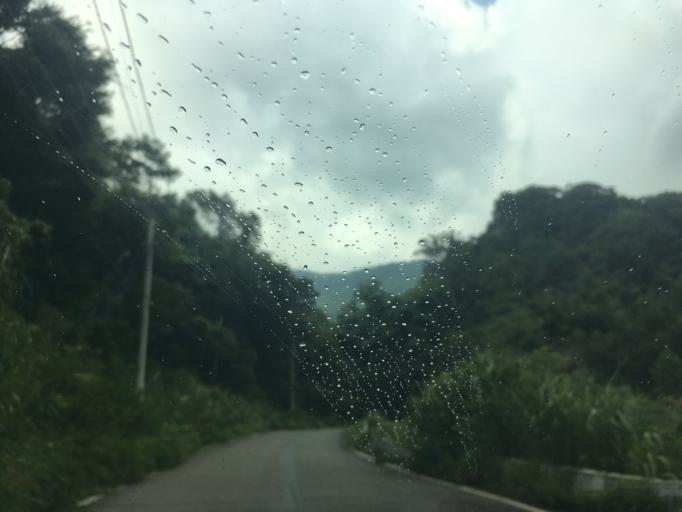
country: TW
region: Taiwan
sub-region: Miaoli
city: Miaoli
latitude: 24.3914
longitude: 120.9731
